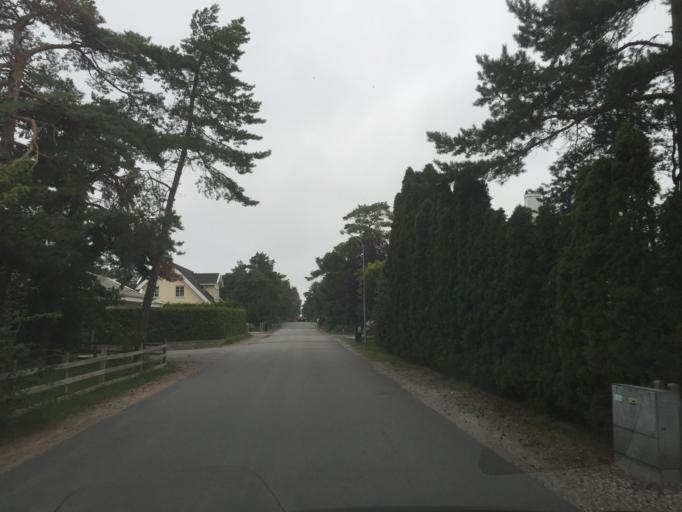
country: SE
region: Skane
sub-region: Vellinge Kommun
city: Hollviken
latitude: 55.4065
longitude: 12.9461
